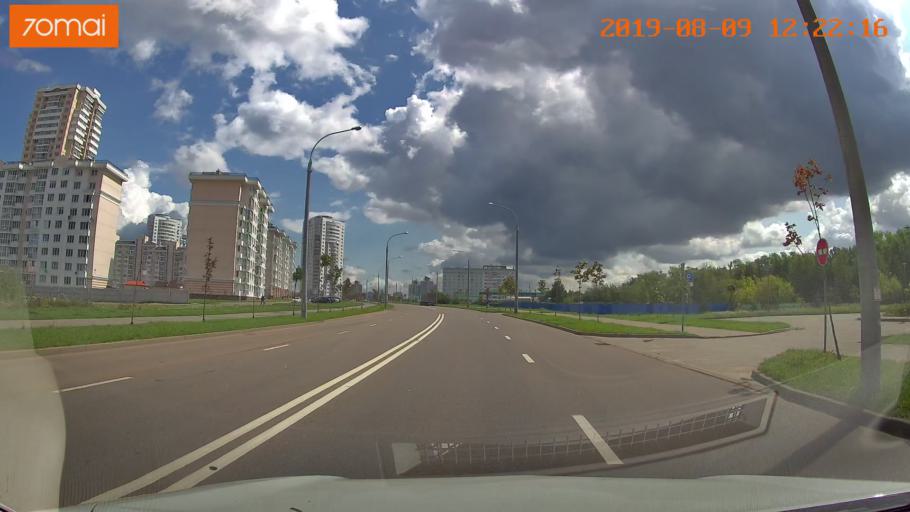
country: BY
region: Minsk
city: Zhdanovichy
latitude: 53.9327
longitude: 27.4691
